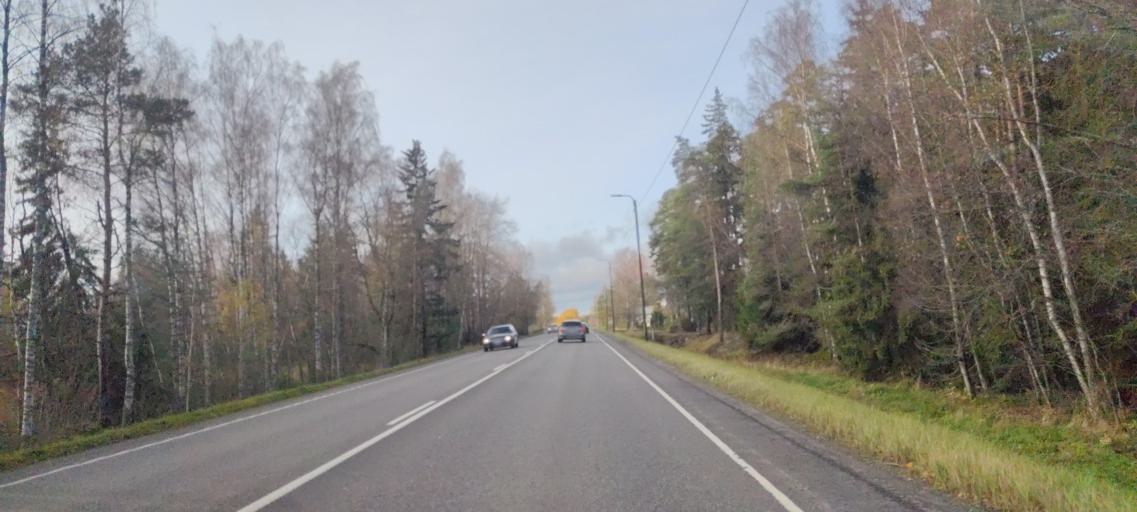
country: FI
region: Varsinais-Suomi
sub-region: Vakka-Suomi
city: Laitila
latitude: 60.8679
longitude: 21.7229
